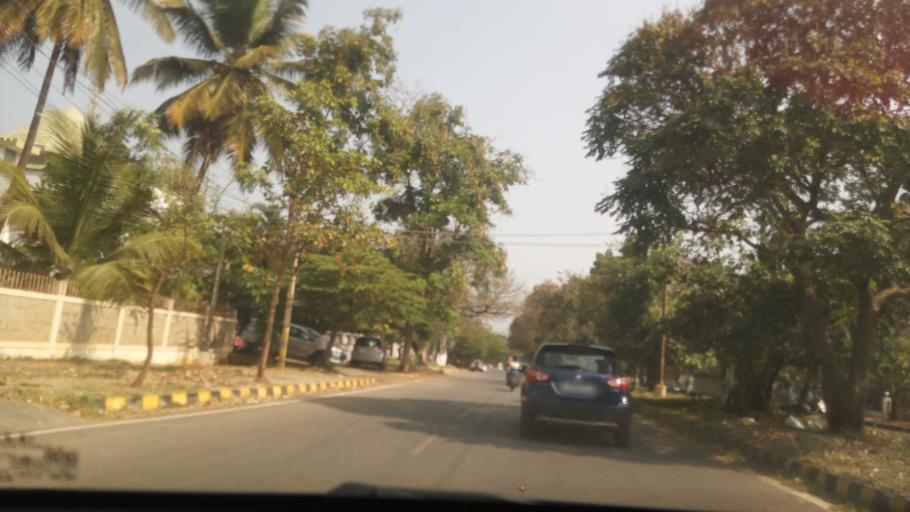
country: IN
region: Karnataka
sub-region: Mysore
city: Mysore
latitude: 12.2920
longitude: 76.6242
